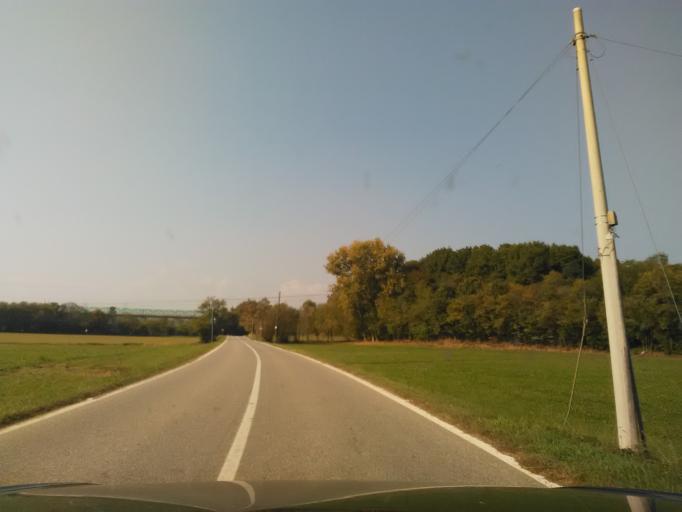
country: IT
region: Piedmont
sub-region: Provincia di Vercelli
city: Santhia
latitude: 45.3944
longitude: 8.1615
